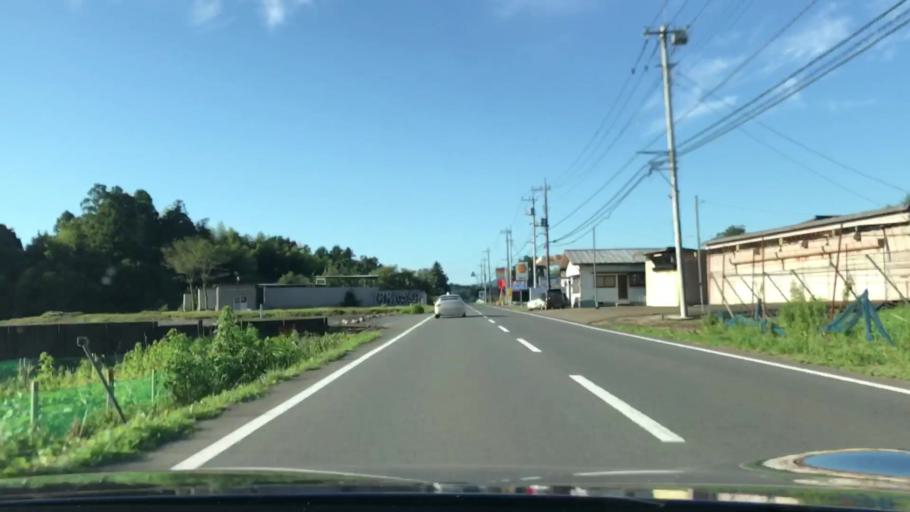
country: JP
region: Ibaraki
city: Makabe
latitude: 36.2432
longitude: 140.1651
